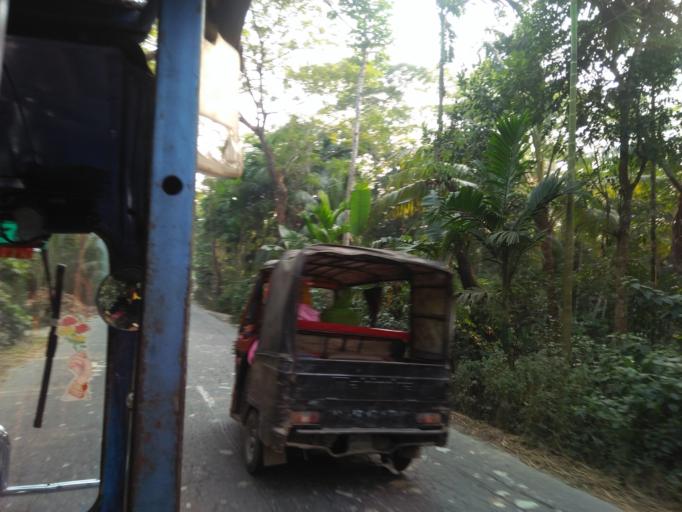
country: BD
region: Barisal
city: Bhola
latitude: 22.7113
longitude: 90.6400
